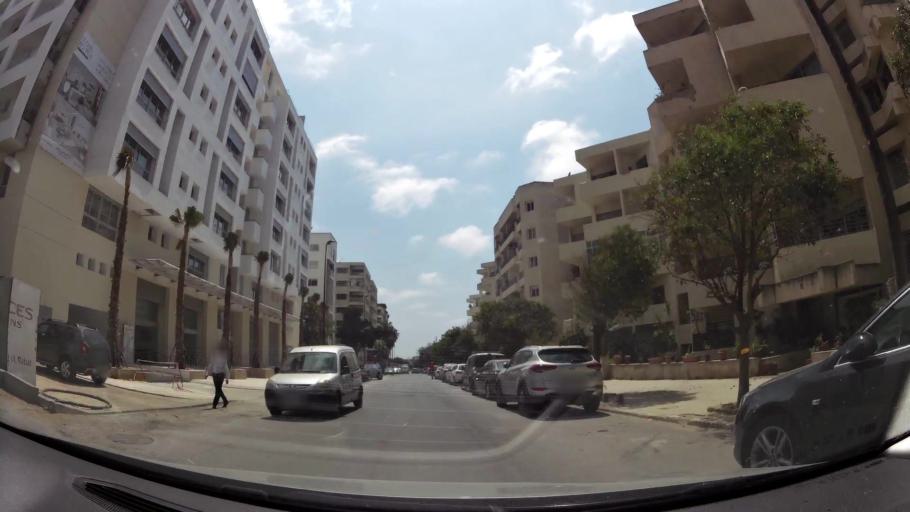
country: MA
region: Rabat-Sale-Zemmour-Zaer
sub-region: Rabat
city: Rabat
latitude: 33.9879
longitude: -6.8485
